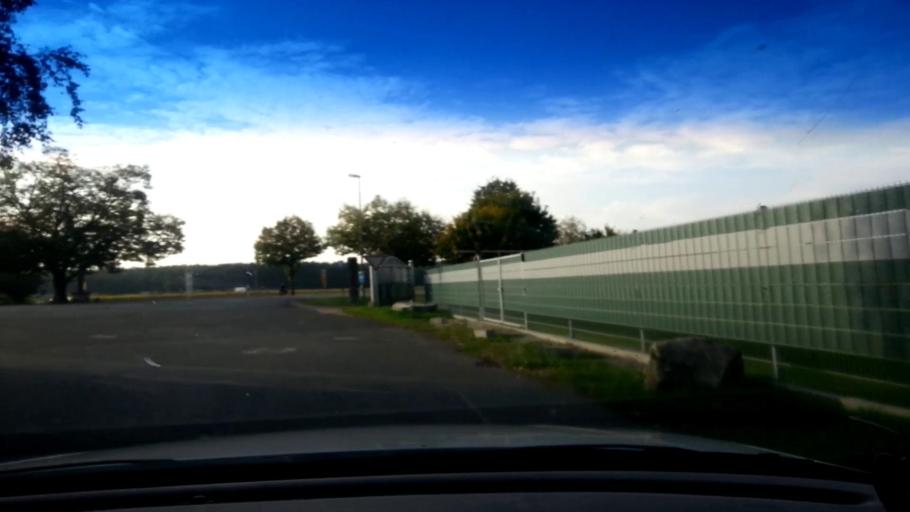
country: DE
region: Bavaria
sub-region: Upper Franconia
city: Hirschaid
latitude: 49.8226
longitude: 10.9854
